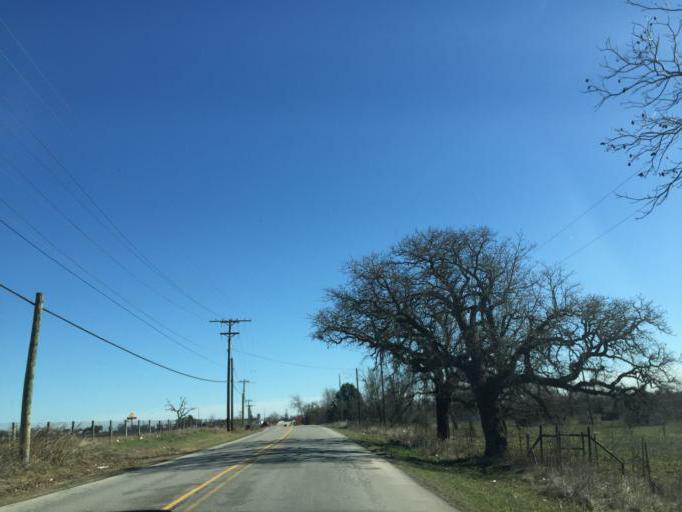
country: US
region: Texas
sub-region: Parker County
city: Hudson Oaks
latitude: 32.7450
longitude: -97.7508
